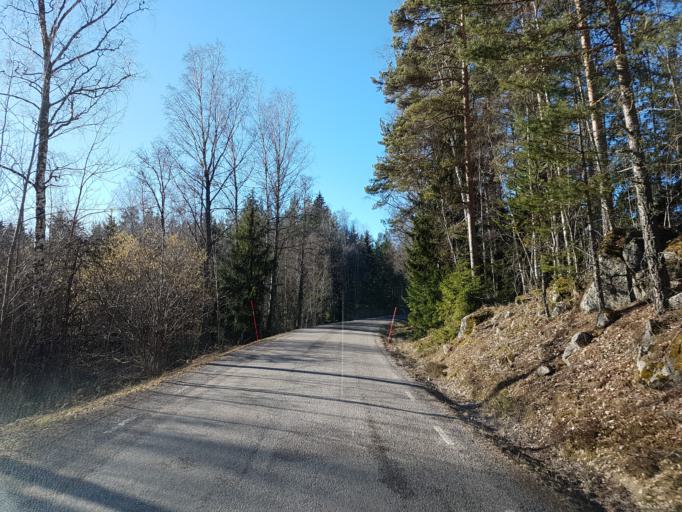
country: SE
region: Kalmar
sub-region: Vasterviks Kommun
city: Overum
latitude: 58.1542
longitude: 16.2808
